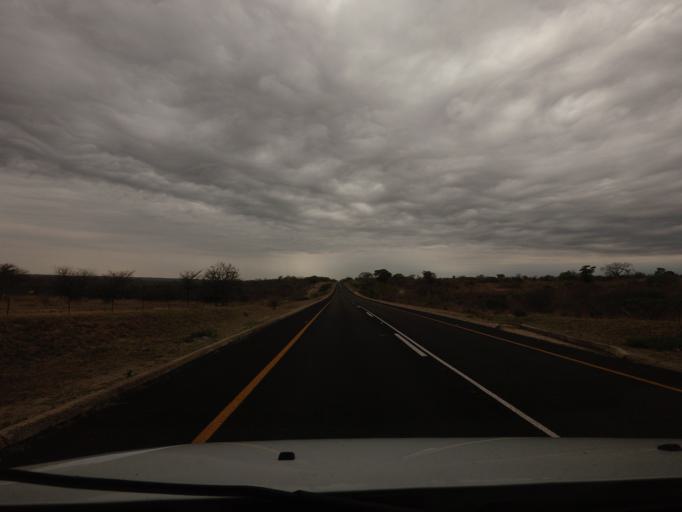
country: ZA
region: Limpopo
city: Thulamahashi
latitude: -24.5677
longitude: 31.0860
